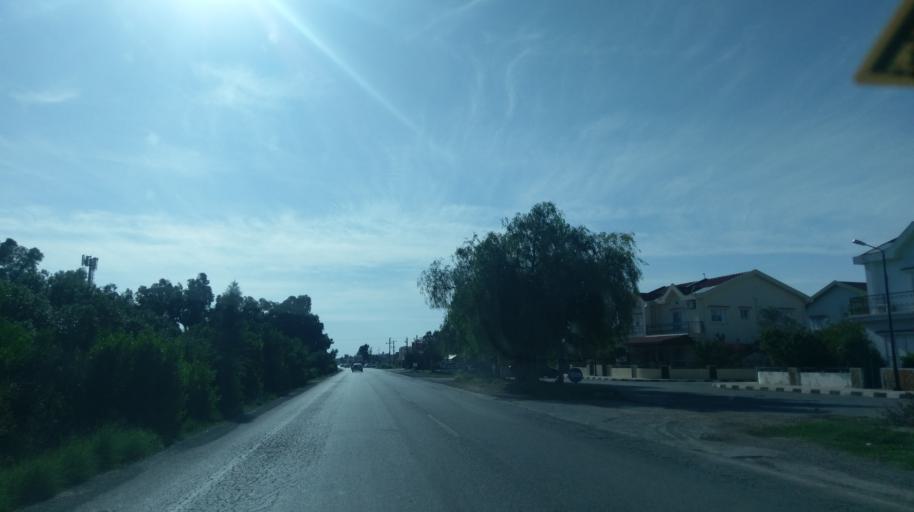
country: CY
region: Ammochostos
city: Trikomo
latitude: 35.2837
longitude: 33.9245
